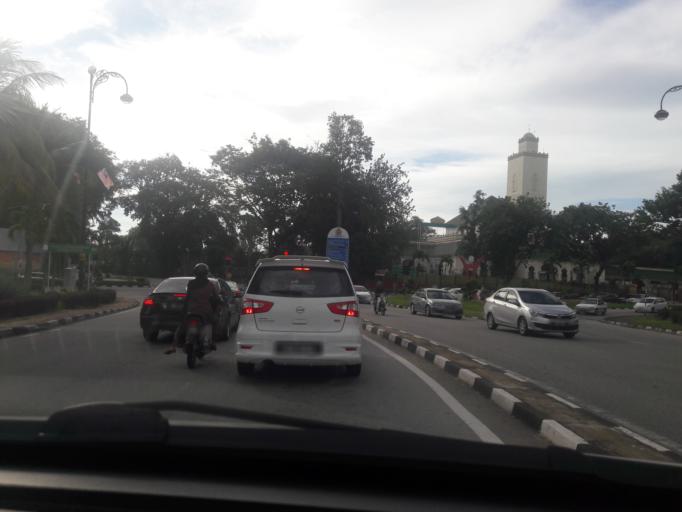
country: MY
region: Kedah
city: Sungai Petani
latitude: 5.6459
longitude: 100.4887
